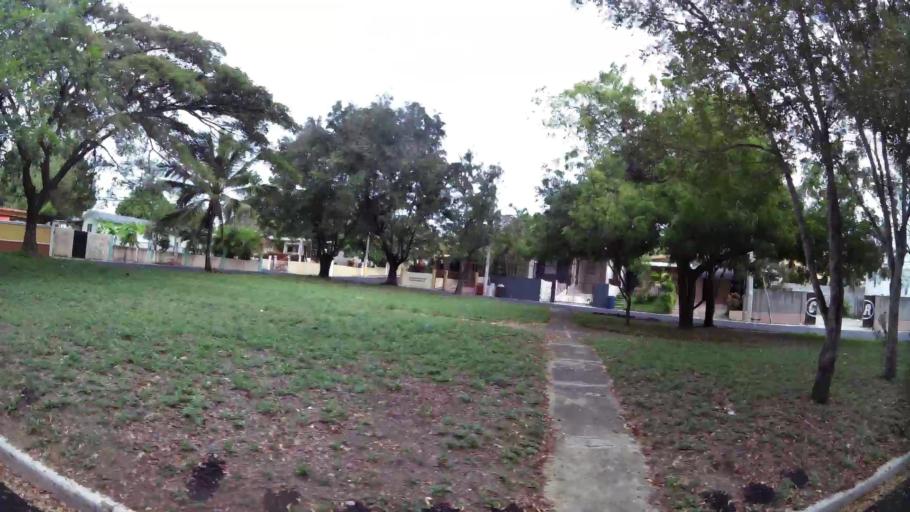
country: DO
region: Santiago
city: Santiago de los Caballeros
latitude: 19.4392
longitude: -70.6703
